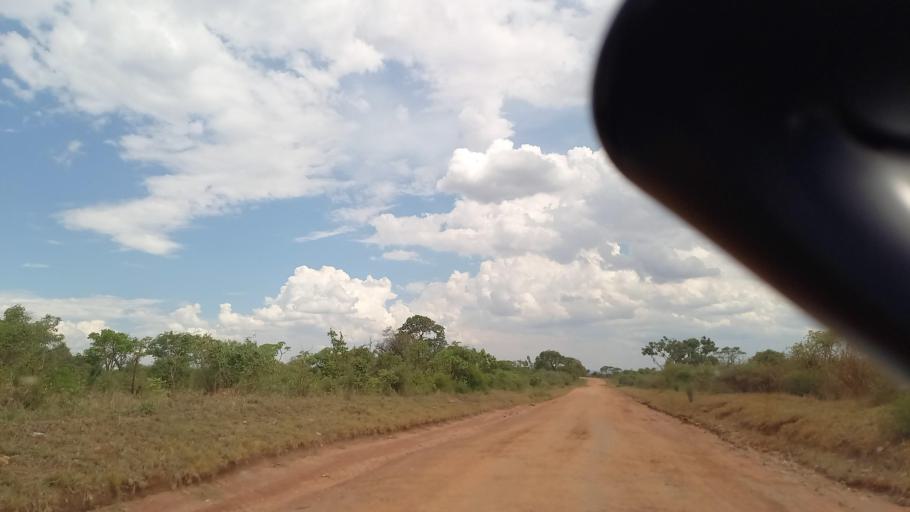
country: ZM
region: Southern
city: Nakambala
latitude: -16.0416
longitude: 27.9737
